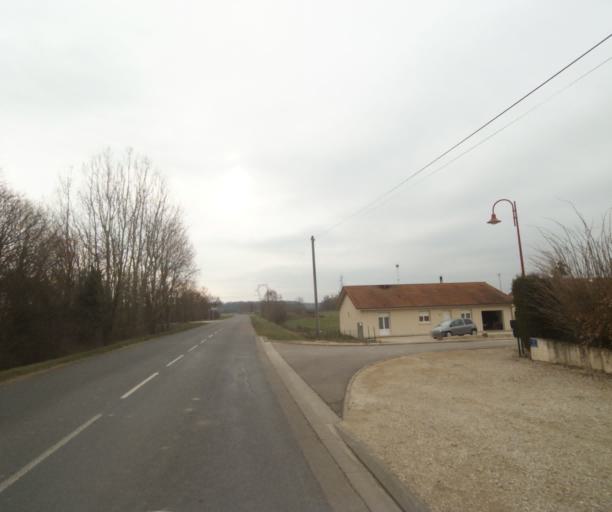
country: FR
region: Champagne-Ardenne
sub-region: Departement de la Marne
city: Pargny-sur-Saulx
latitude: 48.7465
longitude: 4.8486
